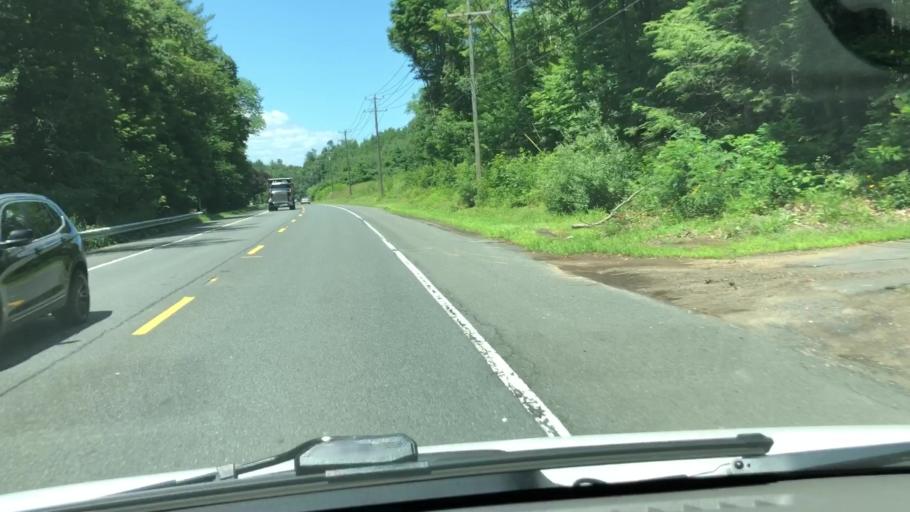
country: US
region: Massachusetts
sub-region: Hampshire County
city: North Amherst
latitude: 42.4404
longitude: -72.5494
